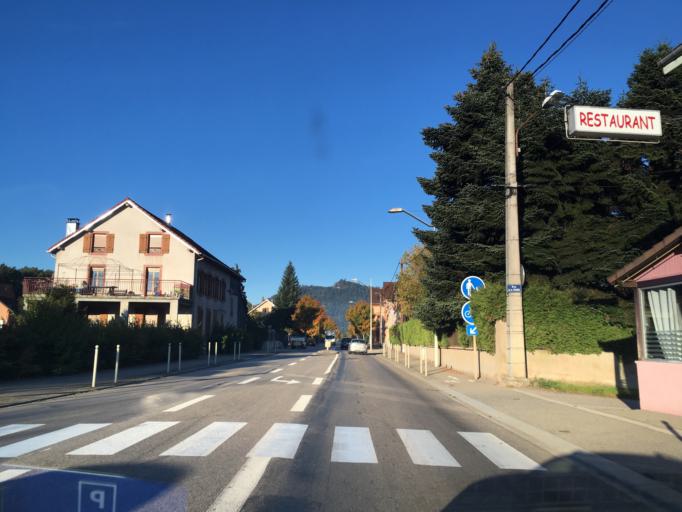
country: FR
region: Lorraine
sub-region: Departement des Vosges
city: Moyenmoutier
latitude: 48.3779
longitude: 6.8890
